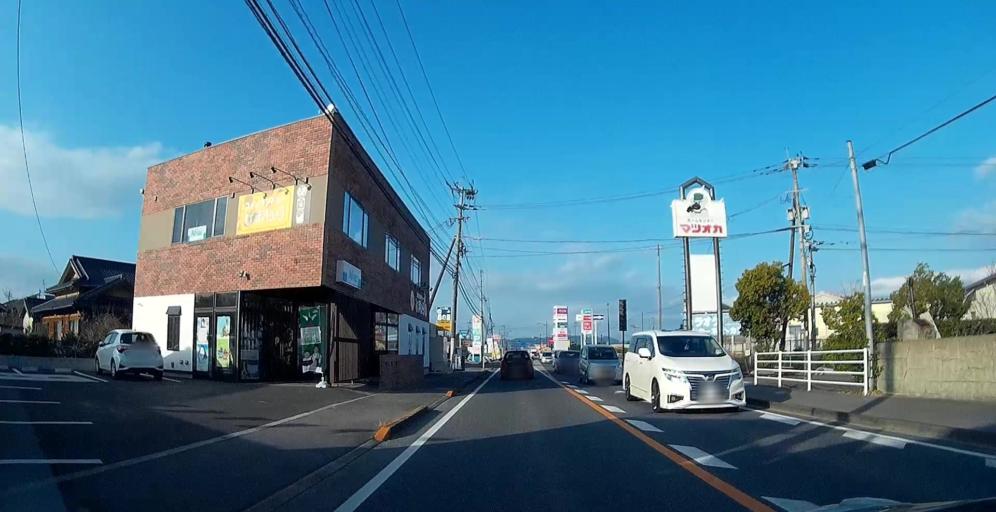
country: JP
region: Kumamoto
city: Matsubase
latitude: 32.5965
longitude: 130.7024
